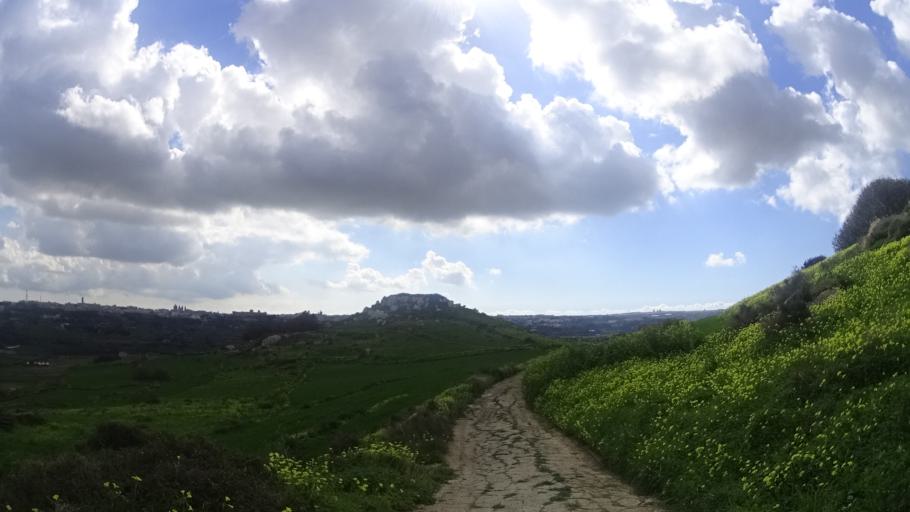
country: MT
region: L-Imtarfa
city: Imtarfa
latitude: 35.9012
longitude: 14.3842
